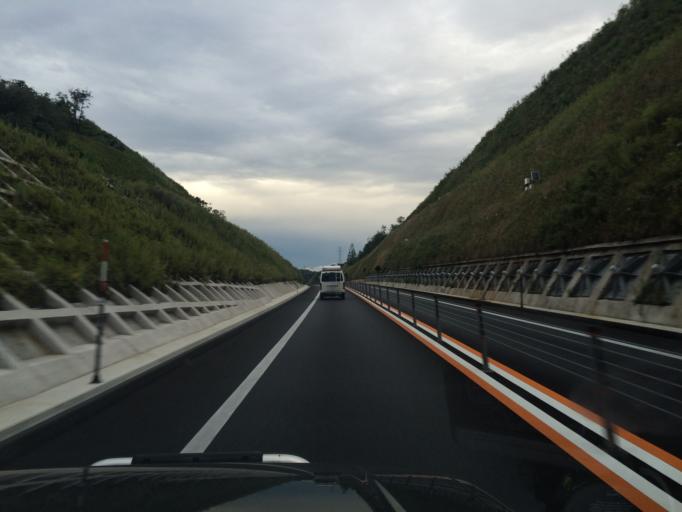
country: JP
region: Tottori
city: Tottori
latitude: 35.4925
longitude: 134.1411
